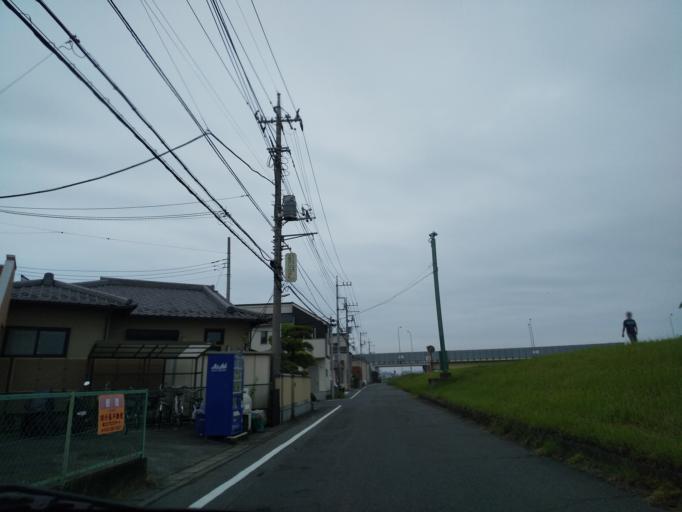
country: JP
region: Tokyo
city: Hino
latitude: 35.6759
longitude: 139.4216
